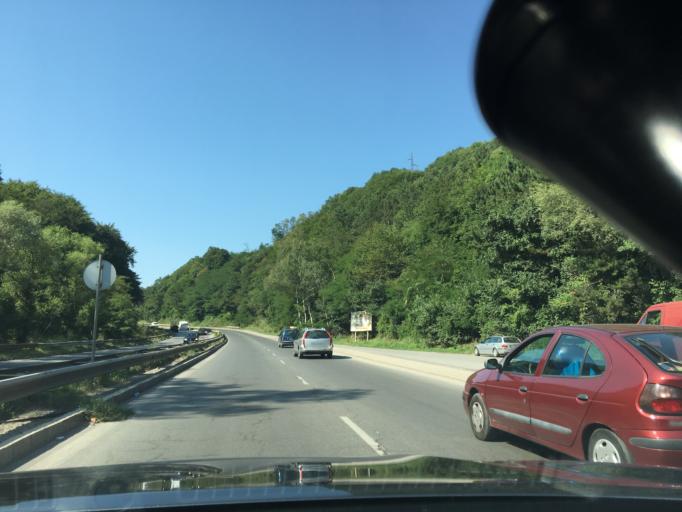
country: BG
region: Sofiya
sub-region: Obshtina Bozhurishte
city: Bozhurishte
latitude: 42.6458
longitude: 23.2068
